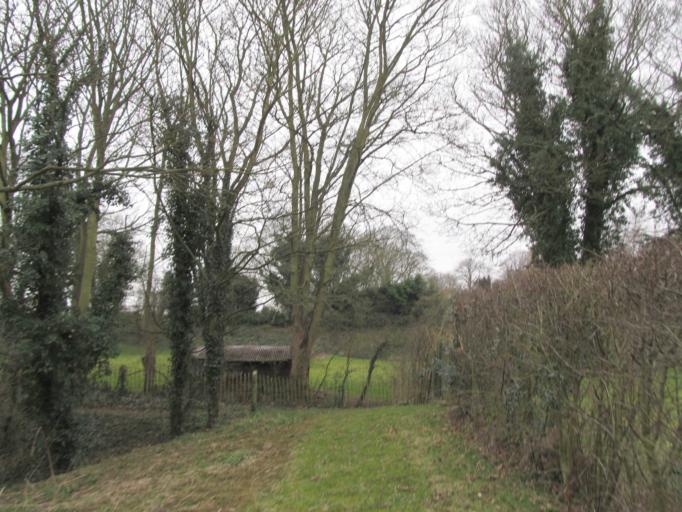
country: GB
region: England
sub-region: Nottinghamshire
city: Misterton
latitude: 53.4074
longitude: -0.8916
